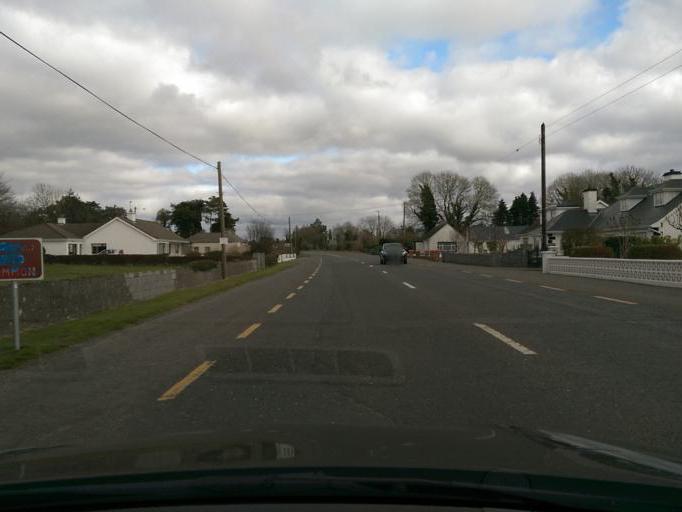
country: IE
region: Connaught
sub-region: County Galway
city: Ballinasloe
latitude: 53.3279
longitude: -8.1725
